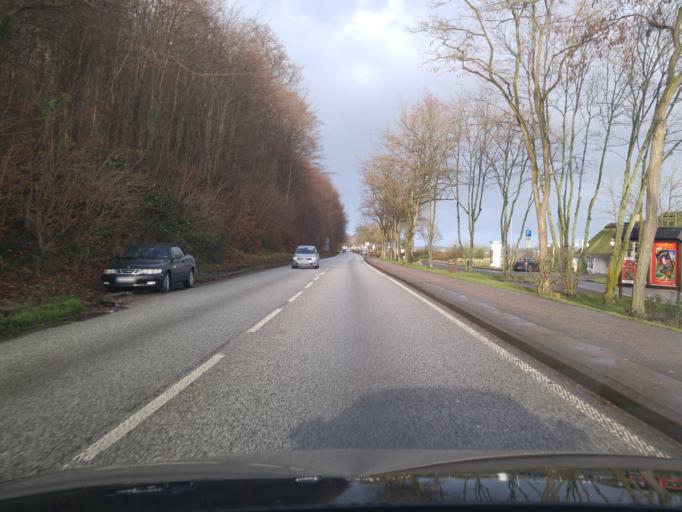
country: DE
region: Schleswig-Holstein
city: Timmendorfer Strand
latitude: 54.0126
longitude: 10.7684
